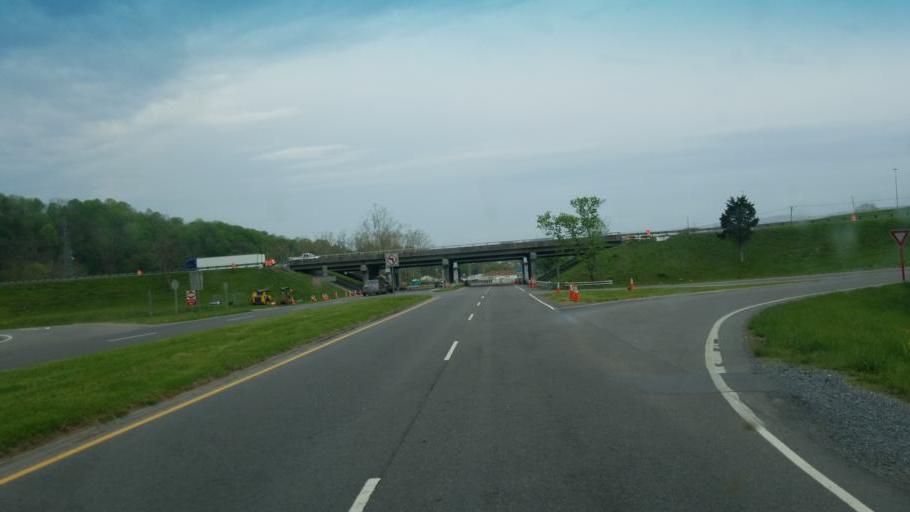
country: US
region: Virginia
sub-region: Smyth County
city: Marion
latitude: 36.8261
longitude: -81.5055
